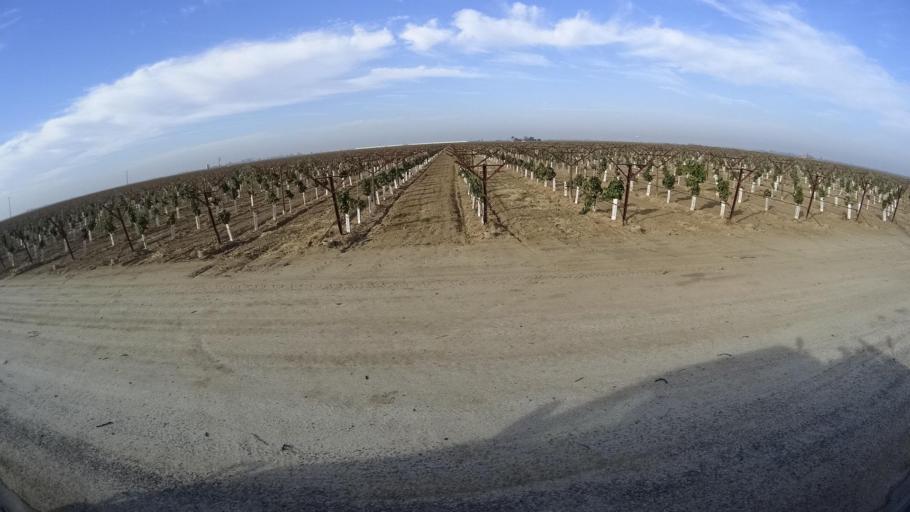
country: US
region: California
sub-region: Kern County
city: Delano
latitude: 35.7308
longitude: -119.2052
